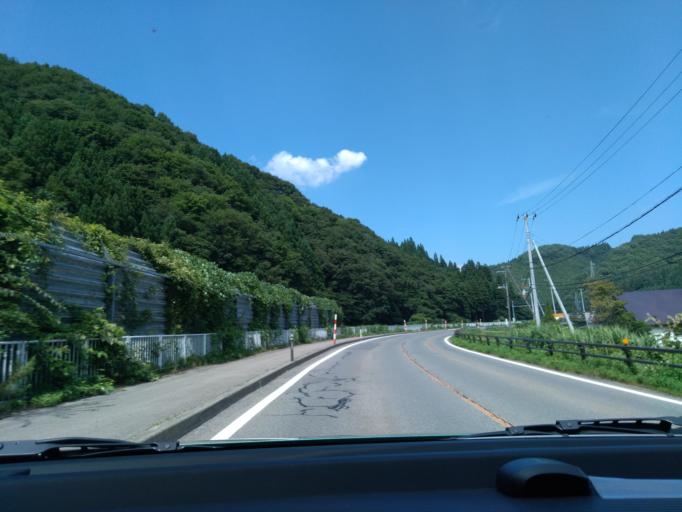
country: JP
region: Akita
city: Kakunodatemachi
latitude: 39.6350
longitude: 140.6545
